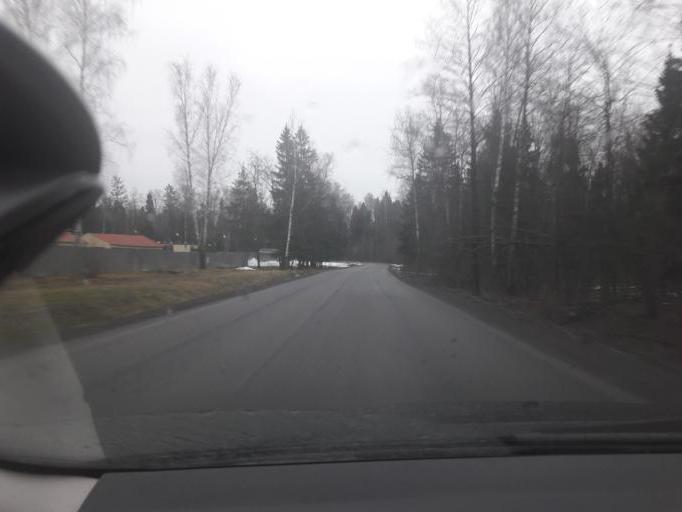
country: RU
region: Moskovskaya
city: Fryazevo
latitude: 55.7603
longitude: 38.5150
